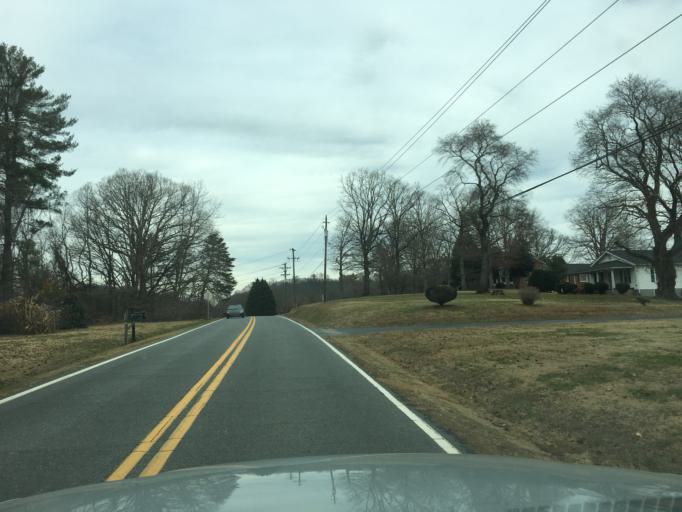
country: US
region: North Carolina
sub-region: McDowell County
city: West Marion
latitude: 35.6181
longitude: -81.9814
